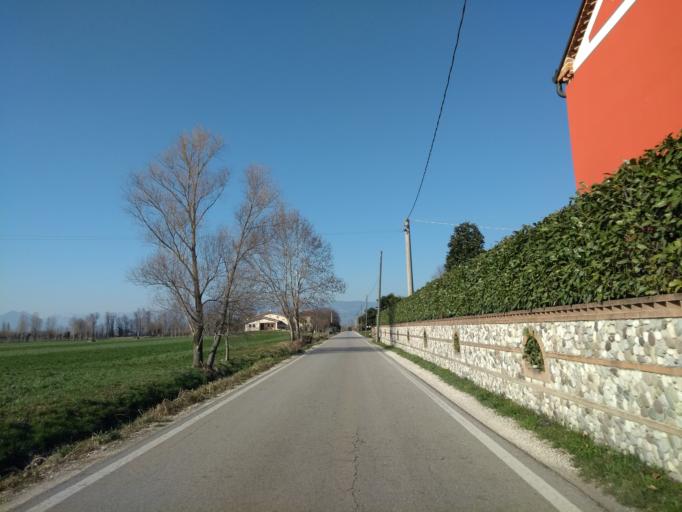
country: IT
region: Veneto
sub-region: Provincia di Padova
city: San Pietro in Gu
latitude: 45.6112
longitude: 11.6501
